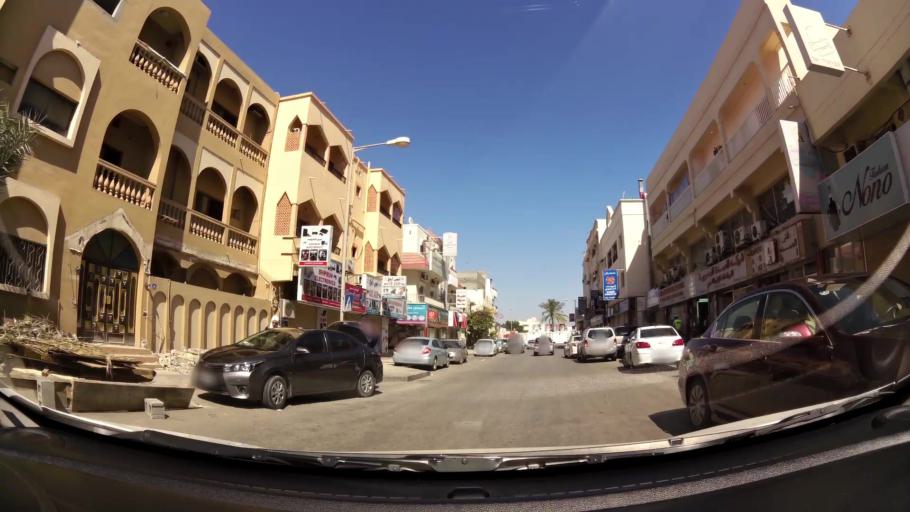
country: BH
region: Muharraq
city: Al Muharraq
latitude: 26.2577
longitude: 50.6188
